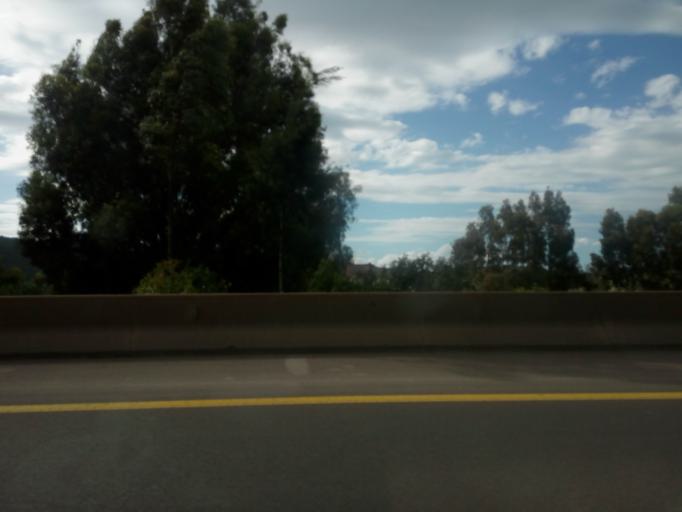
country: DZ
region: Tipaza
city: El Affroun
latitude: 36.4328
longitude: 2.5716
